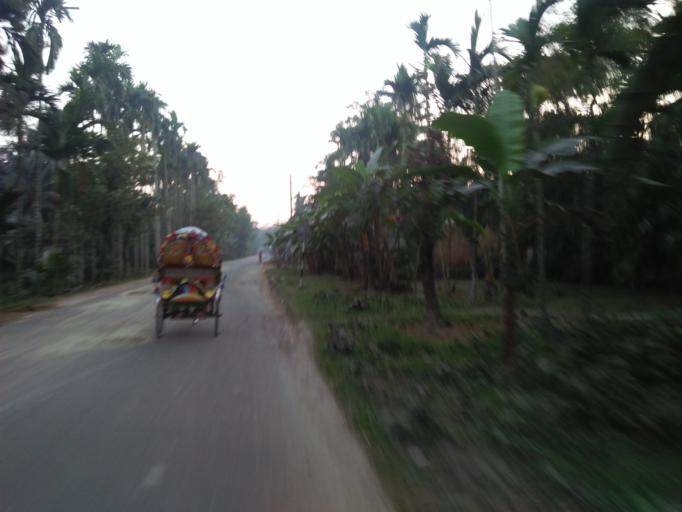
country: BD
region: Barisal
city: Bhola
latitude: 22.7552
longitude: 90.6364
